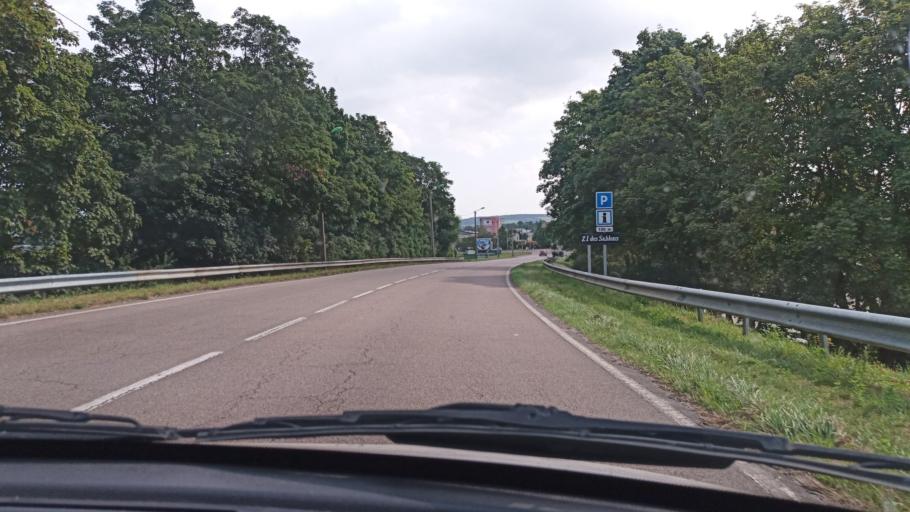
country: FR
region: Bourgogne
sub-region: Departement de l'Yonne
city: Saint-Martin-du-Tertre
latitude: 48.2064
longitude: 3.2668
